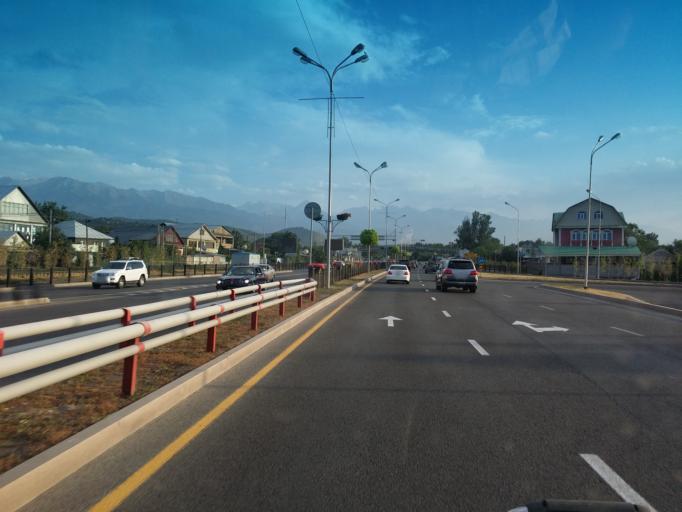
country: KZ
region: Almaty Qalasy
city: Almaty
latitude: 43.2818
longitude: 76.9863
